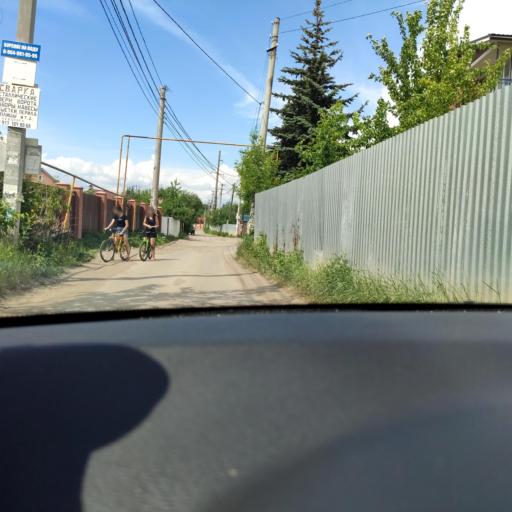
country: RU
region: Samara
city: Novokuybyshevsk
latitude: 53.1468
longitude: 50.0147
